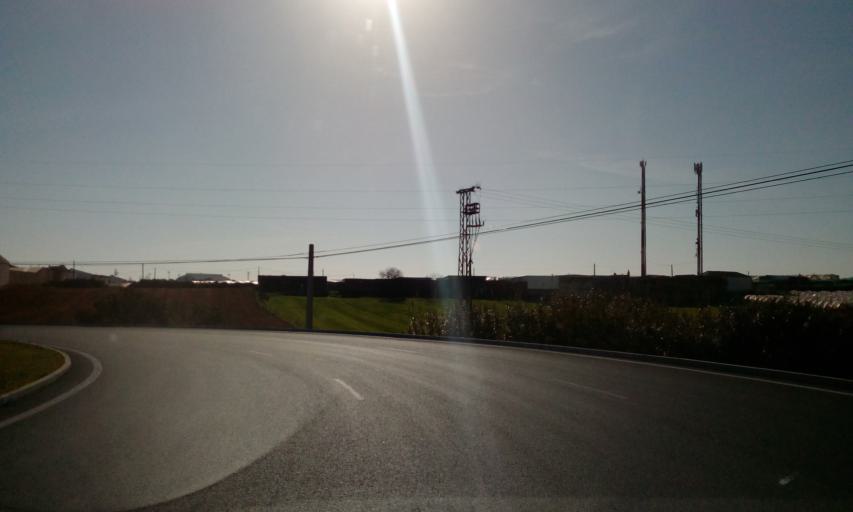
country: ES
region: Andalusia
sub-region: Provincia de Huelva
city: Lepe
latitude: 37.2530
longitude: -7.2115
